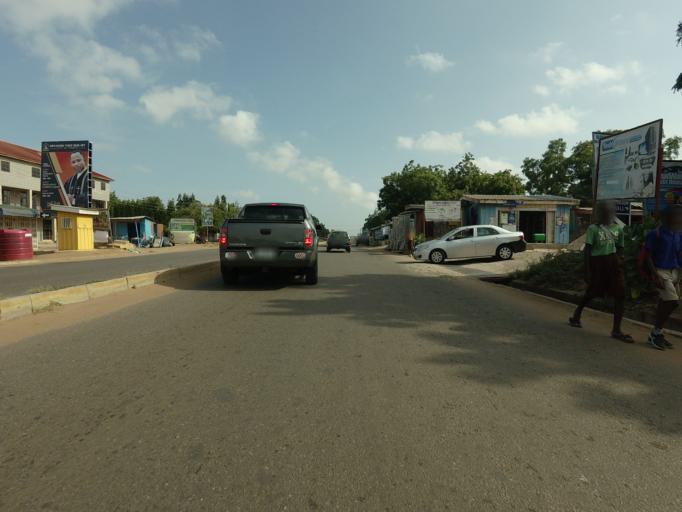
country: GH
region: Greater Accra
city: Tema
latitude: 5.6621
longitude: -0.0507
